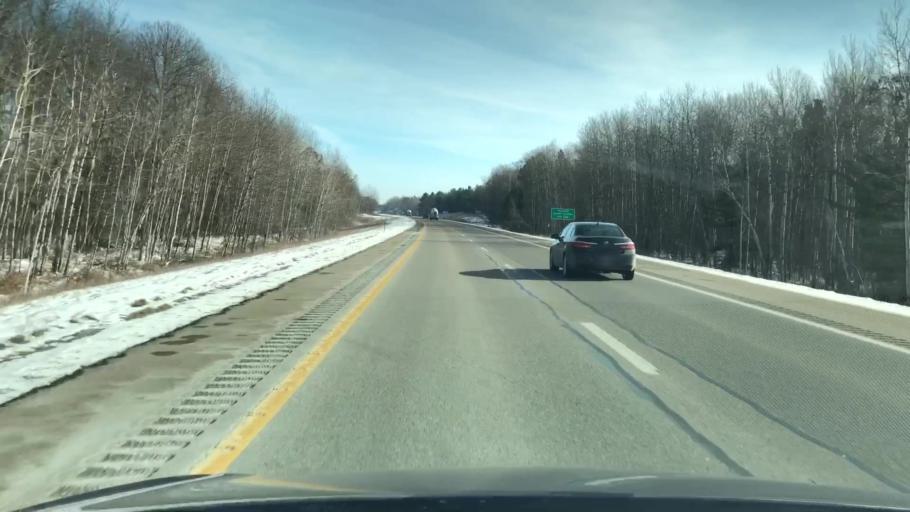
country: US
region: Michigan
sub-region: Roscommon County
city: Saint Helen
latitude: 44.3124
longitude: -84.4298
